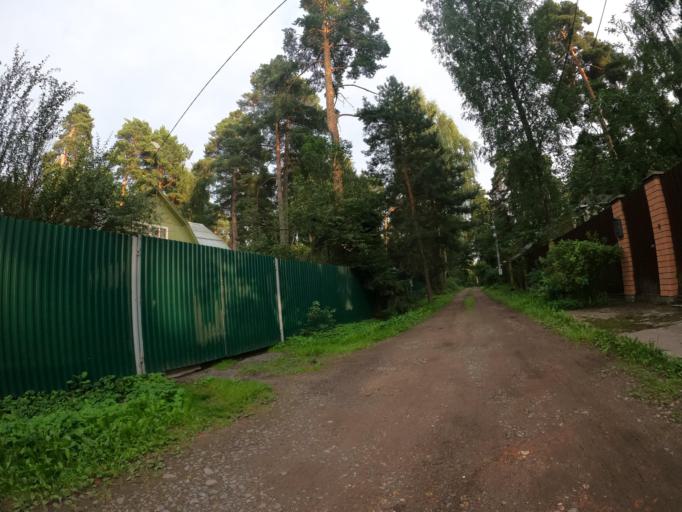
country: RU
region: Moskovskaya
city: Bykovo
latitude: 55.6385
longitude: 38.0959
